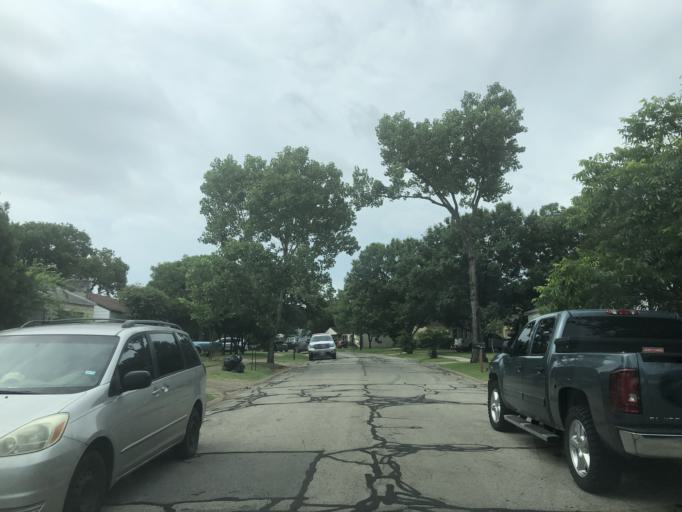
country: US
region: Texas
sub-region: Dallas County
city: Irving
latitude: 32.8047
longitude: -96.9509
